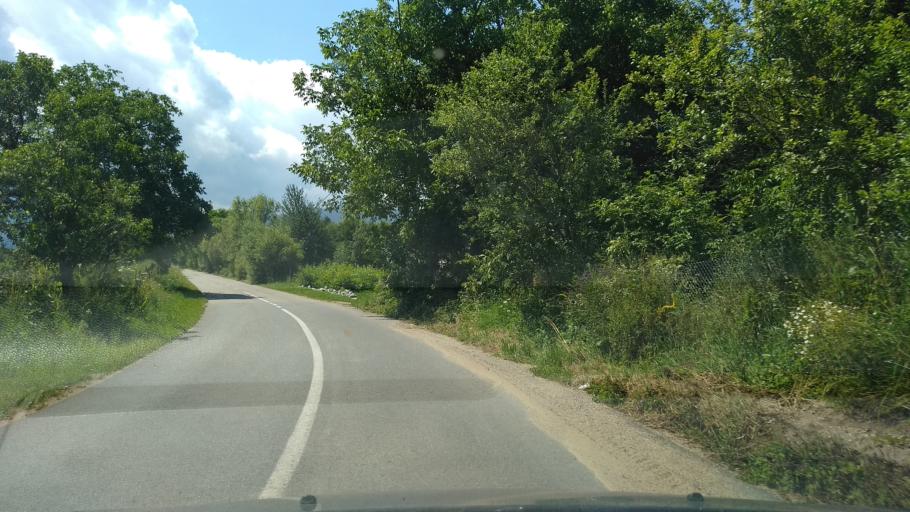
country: RO
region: Hunedoara
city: Salasu de Sus
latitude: 45.5058
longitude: 22.9510
